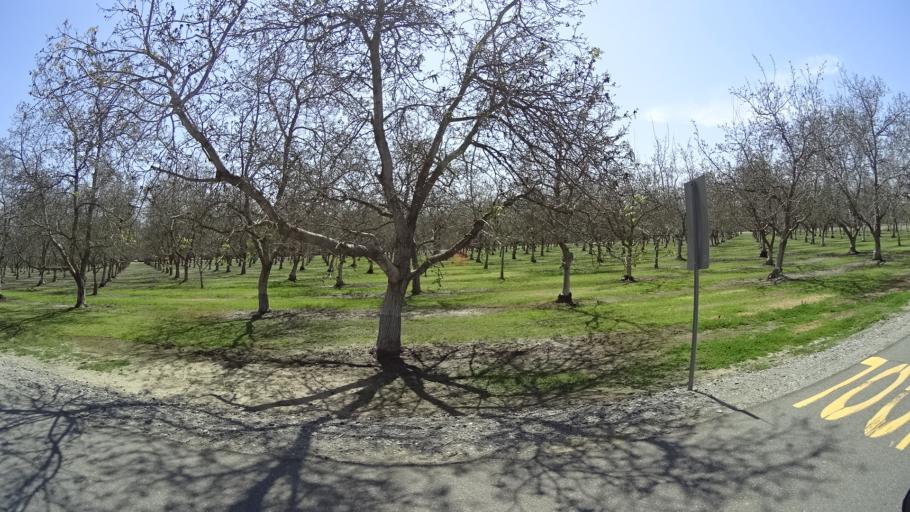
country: US
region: California
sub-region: Glenn County
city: Willows
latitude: 39.5345
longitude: -122.0093
